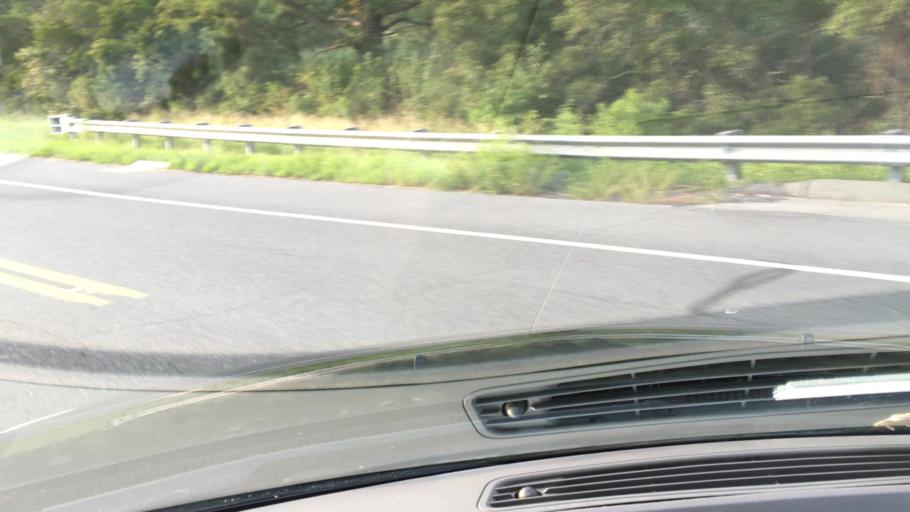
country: US
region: Delaware
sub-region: Sussex County
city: Bethany Beach
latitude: 38.5229
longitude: -75.0704
